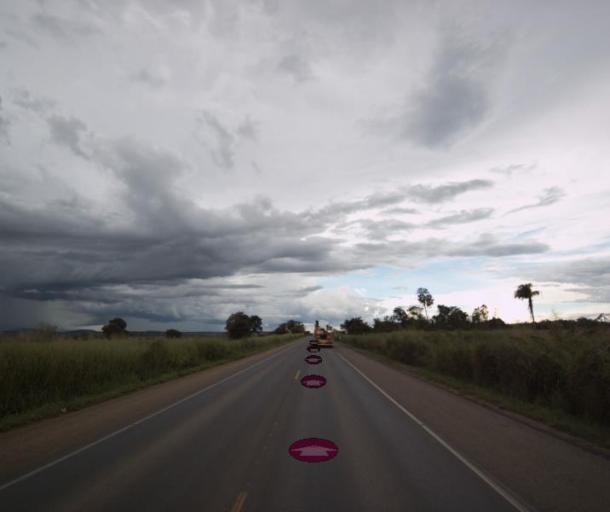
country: BR
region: Goias
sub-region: Itapaci
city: Itapaci
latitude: -15.0151
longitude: -49.4211
